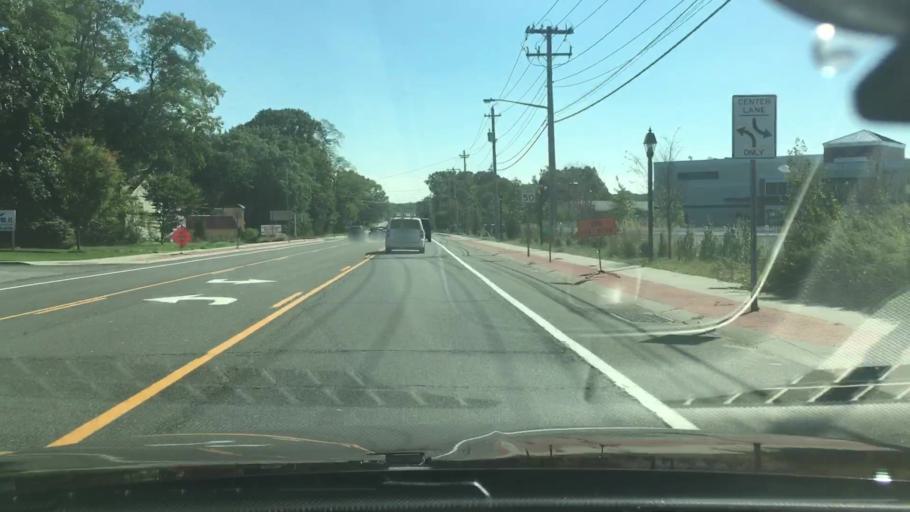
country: US
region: New York
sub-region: Suffolk County
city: Port Jefferson Station
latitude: 40.9185
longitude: -73.0384
